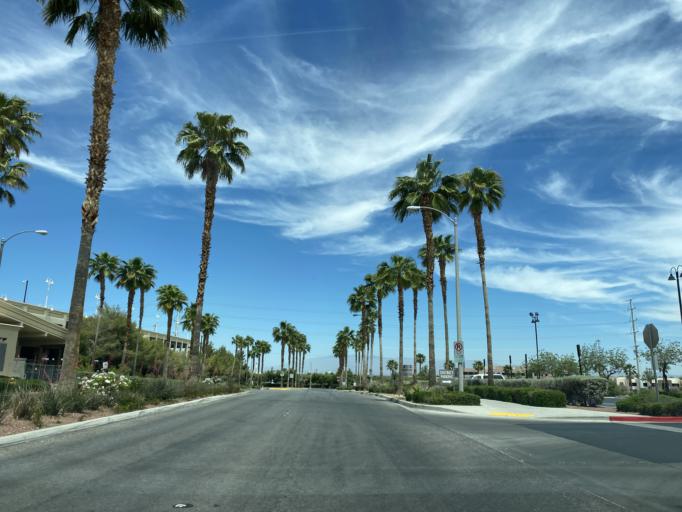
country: US
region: Nevada
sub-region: Clark County
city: Whitney
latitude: 36.0215
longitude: -115.0885
